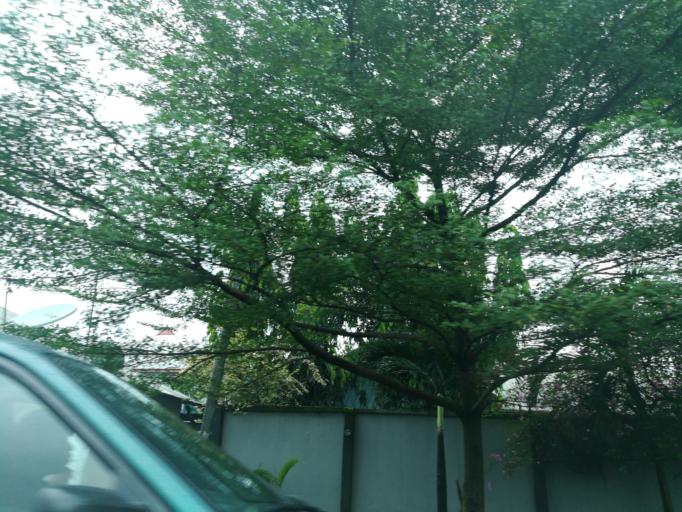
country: NG
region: Rivers
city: Port Harcourt
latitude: 4.8191
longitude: 7.0161
